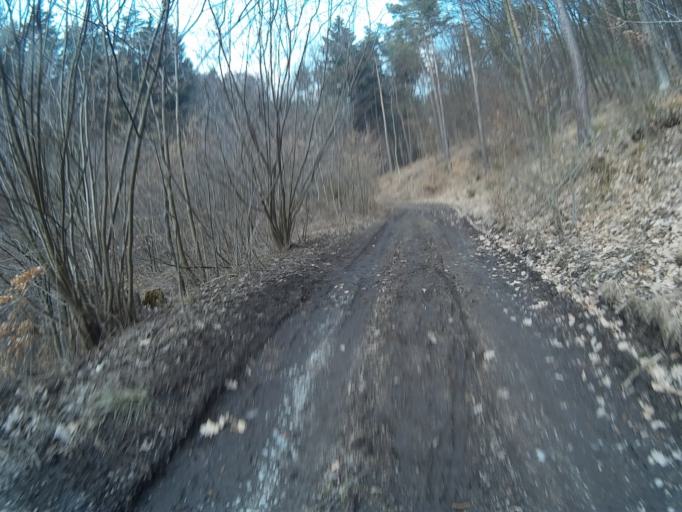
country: CZ
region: South Moravian
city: Pozorice
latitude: 49.2274
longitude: 16.8051
